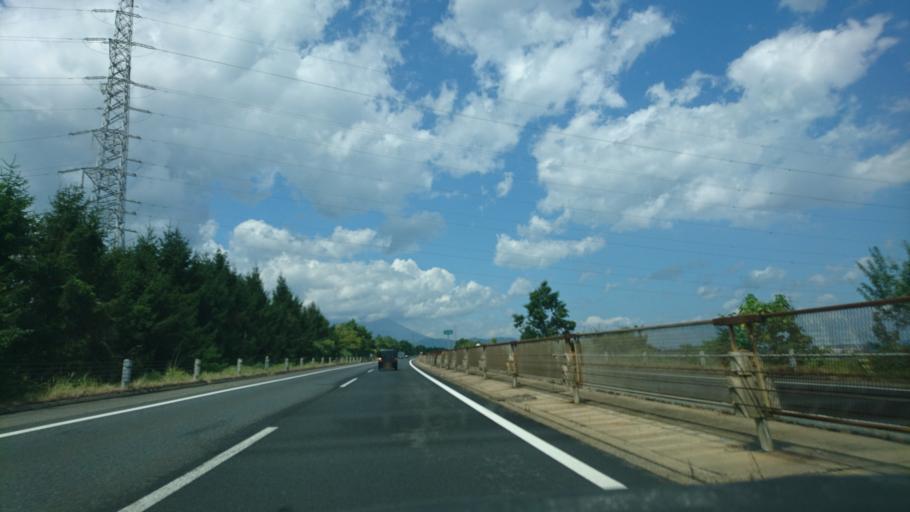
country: JP
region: Iwate
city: Morioka-shi
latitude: 39.6747
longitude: 141.1049
